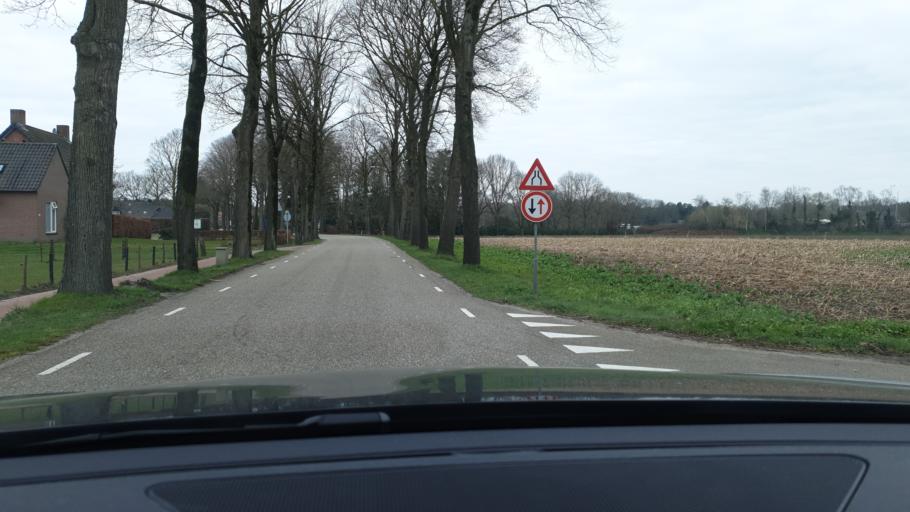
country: NL
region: North Brabant
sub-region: Gemeente Eersel
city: Eersel
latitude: 51.4152
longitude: 5.3017
